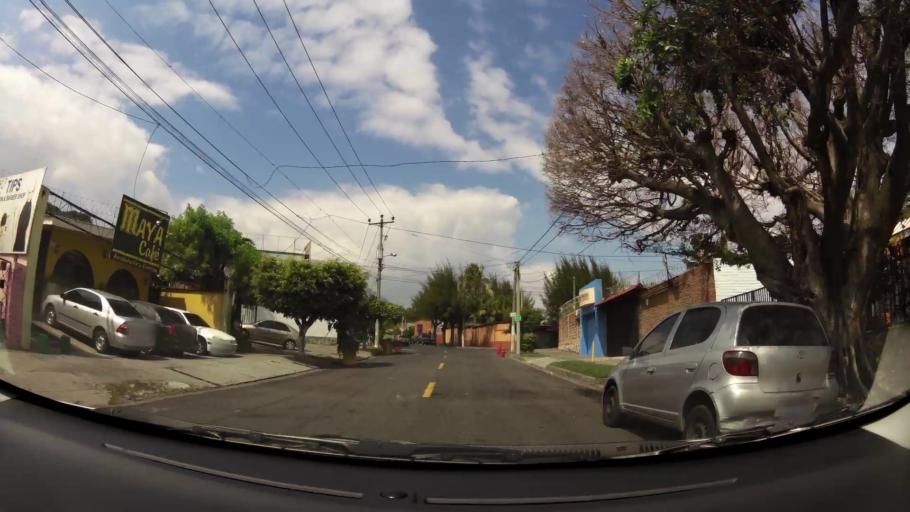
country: SV
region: San Salvador
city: Mejicanos
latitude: 13.7068
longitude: -89.2195
